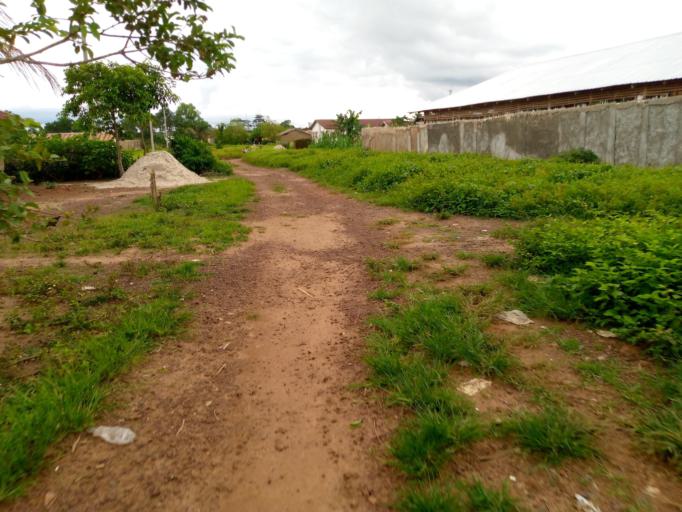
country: SL
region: Southern Province
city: Moyamba
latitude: 8.1521
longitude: -12.4386
